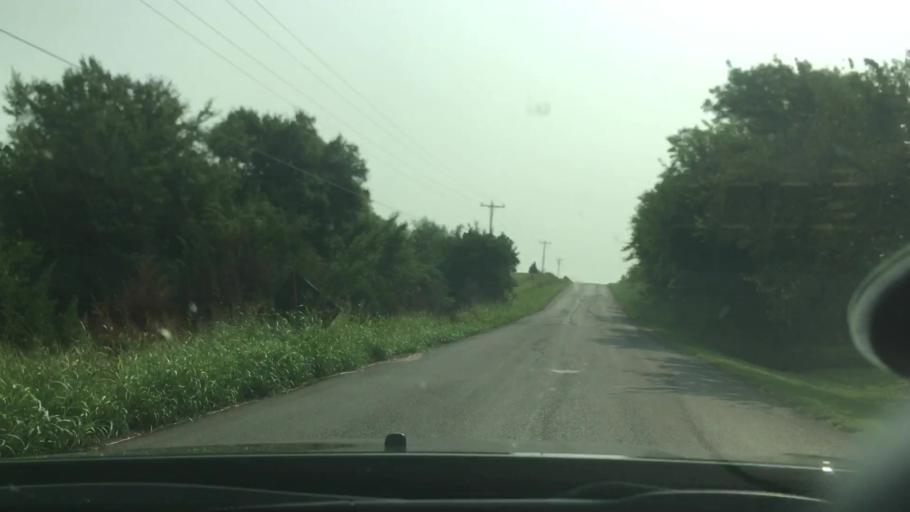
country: US
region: Oklahoma
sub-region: Garvin County
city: Lindsay
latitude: 34.8120
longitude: -97.6427
